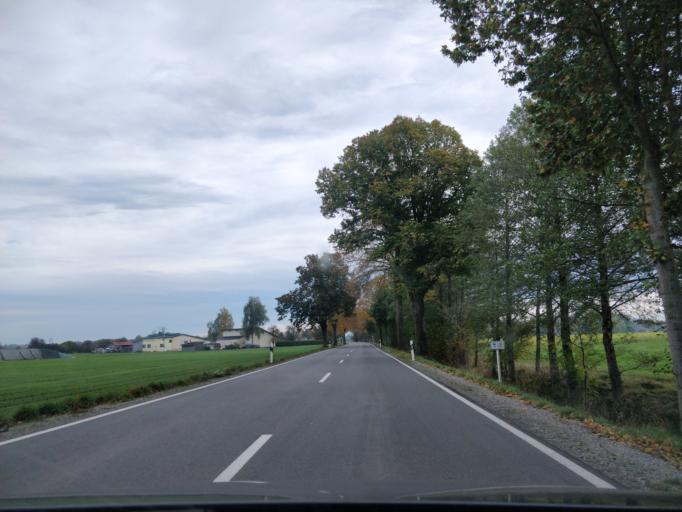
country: DE
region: Bavaria
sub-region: Swabia
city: Wiedergeltingen
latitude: 48.0359
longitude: 10.6832
